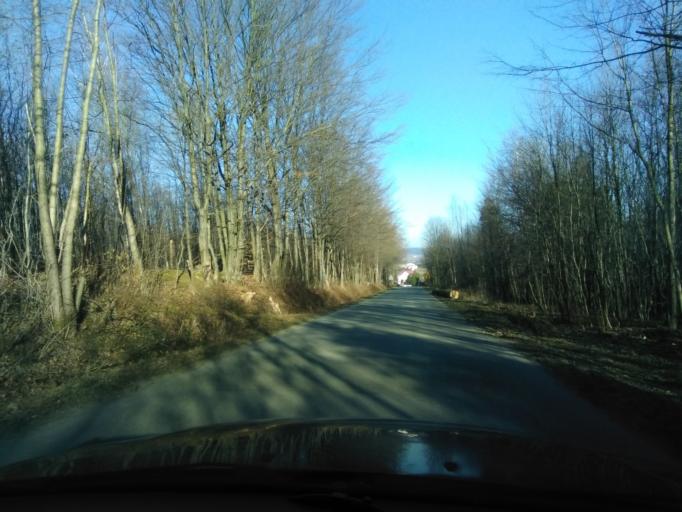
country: PL
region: Subcarpathian Voivodeship
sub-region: Powiat krosnienski
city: Rymanow
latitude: 49.5998
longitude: 21.8961
